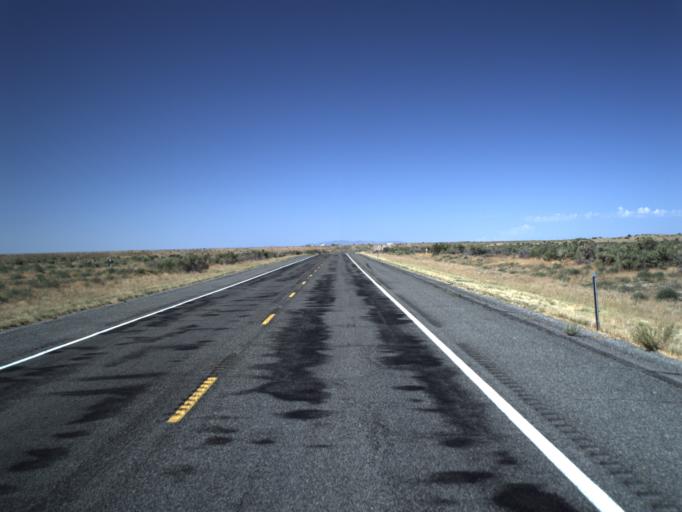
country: US
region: Utah
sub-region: Millard County
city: Delta
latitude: 39.4087
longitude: -112.4897
